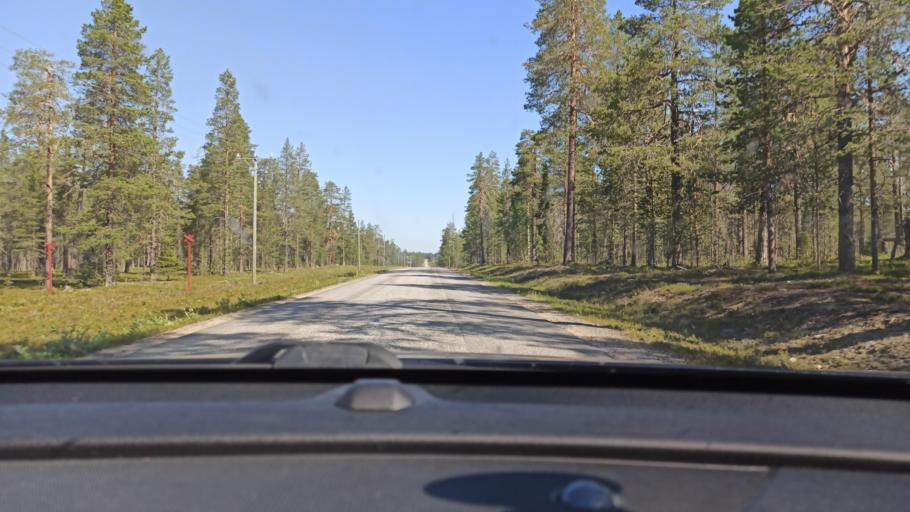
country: FI
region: Lapland
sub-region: Tunturi-Lappi
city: Kolari
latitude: 67.6417
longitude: 24.1582
